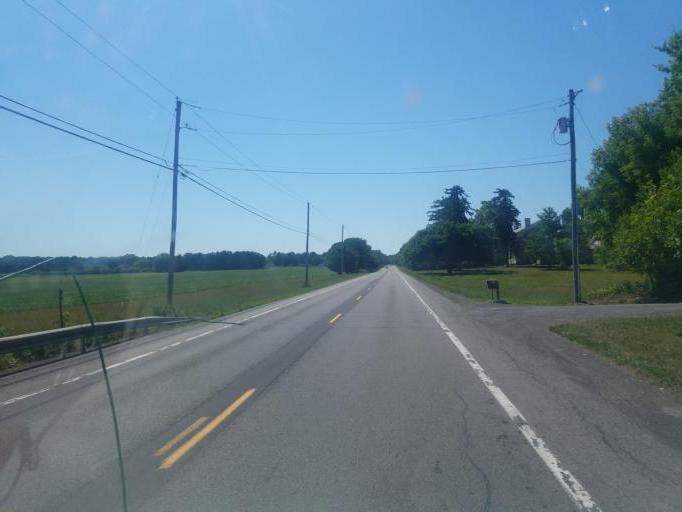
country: US
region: New York
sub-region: Ontario County
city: Phelps
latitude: 42.9480
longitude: -77.0162
